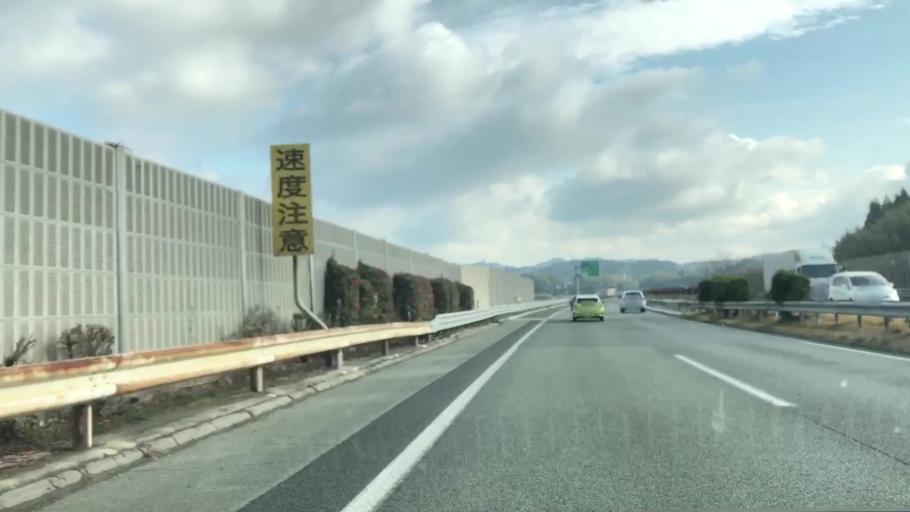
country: JP
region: Kumamoto
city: Tamana
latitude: 32.9962
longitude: 130.5972
